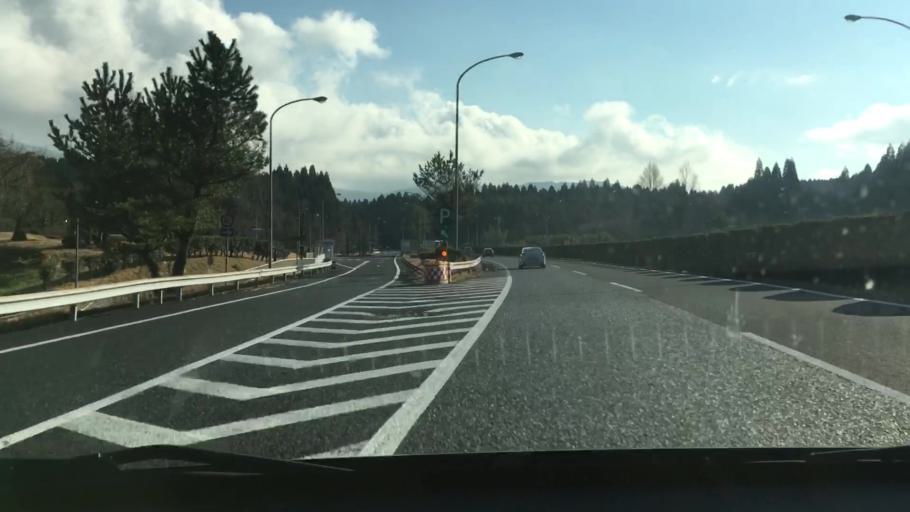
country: JP
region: Kagoshima
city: Okuchi-shinohara
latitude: 32.0075
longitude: 130.7557
